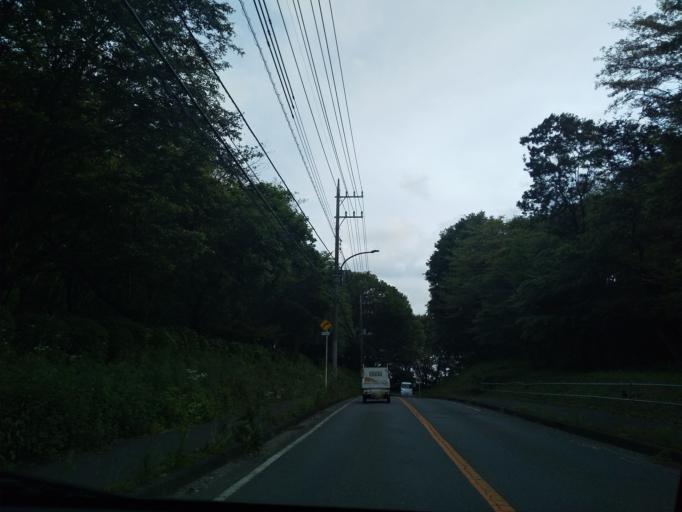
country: JP
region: Kanagawa
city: Zama
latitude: 35.5179
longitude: 139.3949
